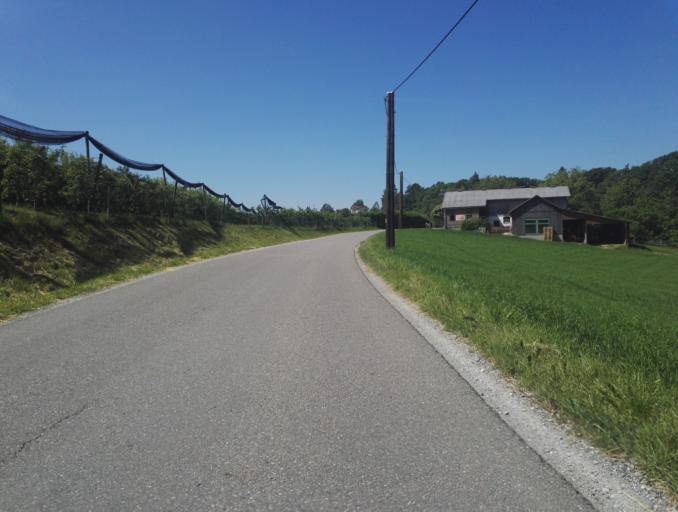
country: AT
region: Styria
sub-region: Politischer Bezirk Graz-Umgebung
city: Hart bei Graz
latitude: 47.0458
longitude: 15.5561
